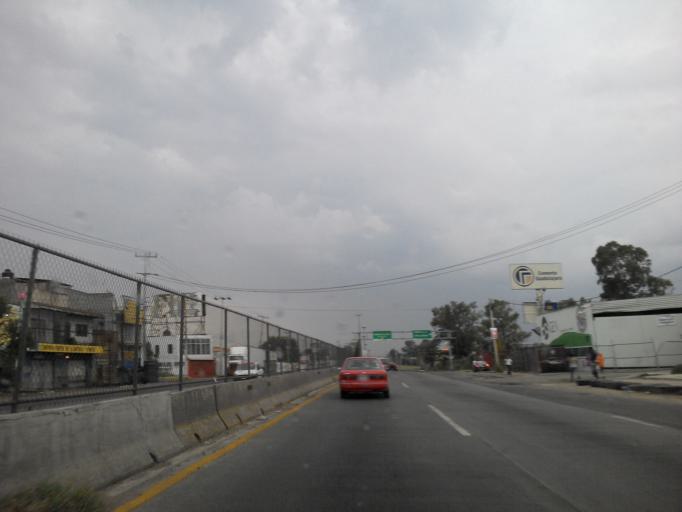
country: MX
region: Jalisco
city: Tlaquepaque
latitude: 20.6126
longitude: -103.2827
